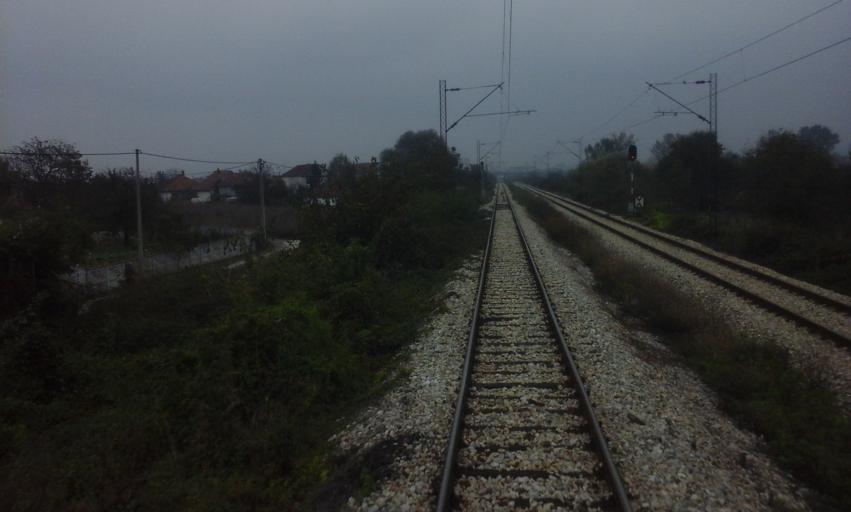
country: RS
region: Central Serbia
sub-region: Pomoravski Okrug
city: Jagodina
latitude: 43.9922
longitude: 21.2439
